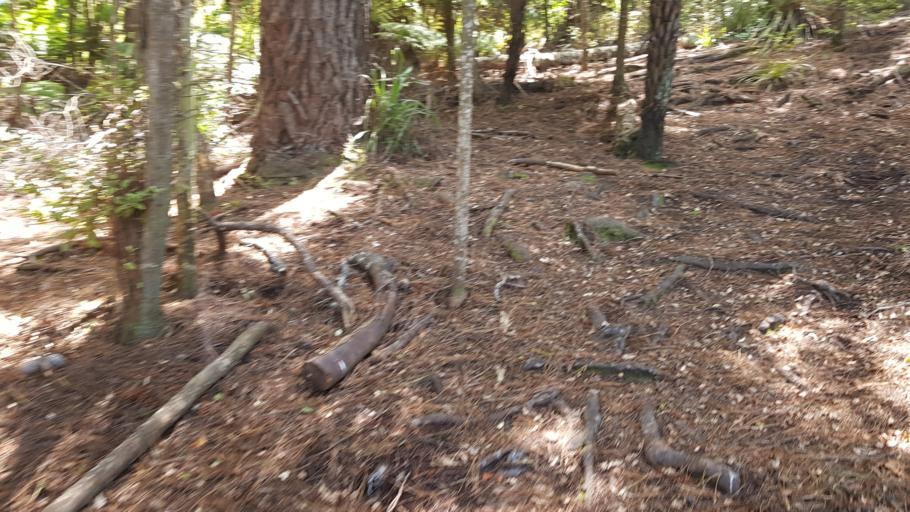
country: NZ
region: Auckland
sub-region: Auckland
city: North Shore
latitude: -36.8238
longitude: 174.7158
